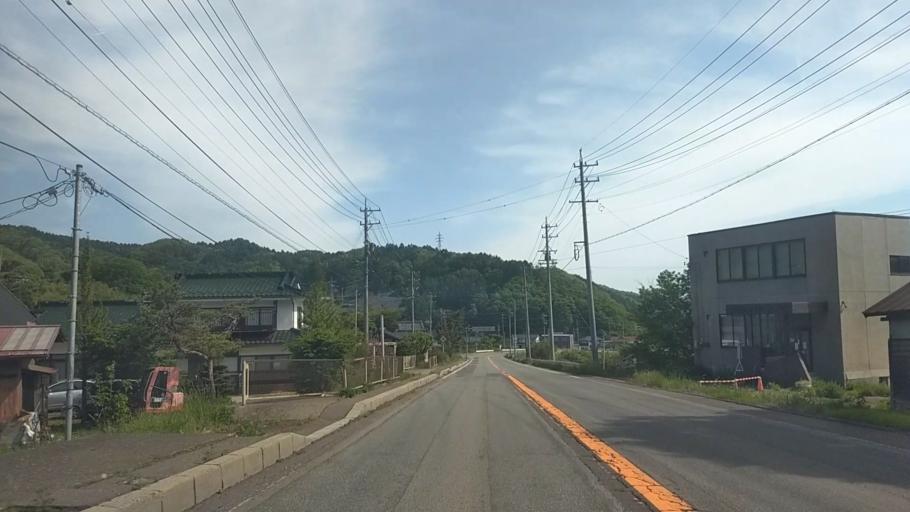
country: JP
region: Nagano
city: Saku
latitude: 36.0565
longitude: 138.4670
